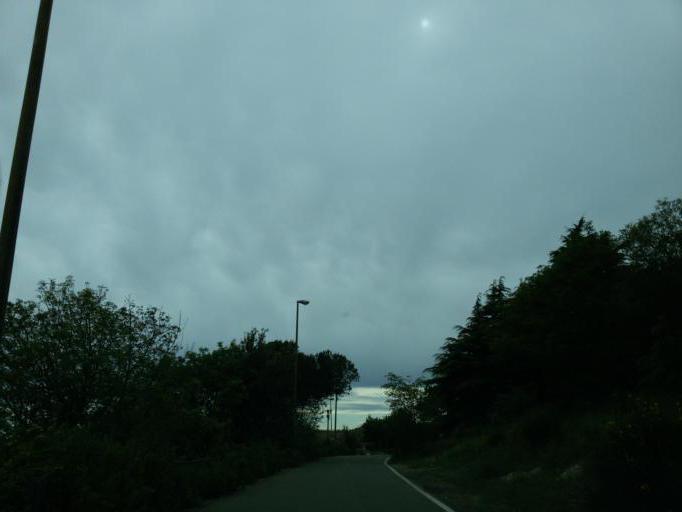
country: IT
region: Liguria
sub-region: Provincia di Genova
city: Genoa
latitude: 44.4378
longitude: 8.9216
